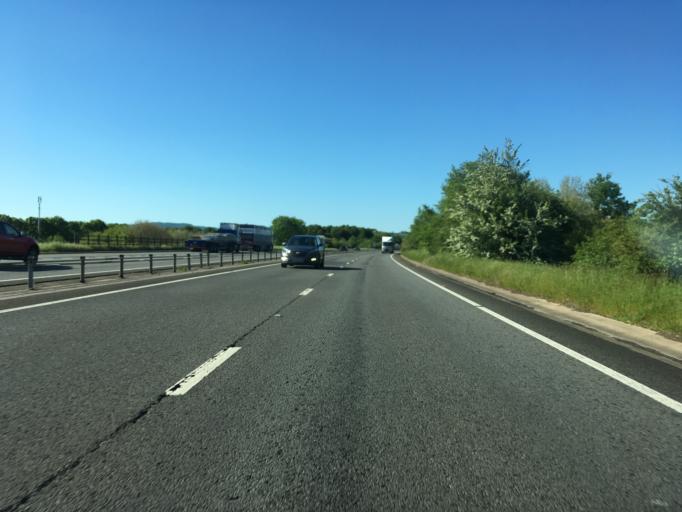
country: GB
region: Wales
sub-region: Monmouthshire
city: Llangwm
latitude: 51.7349
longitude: -2.8420
